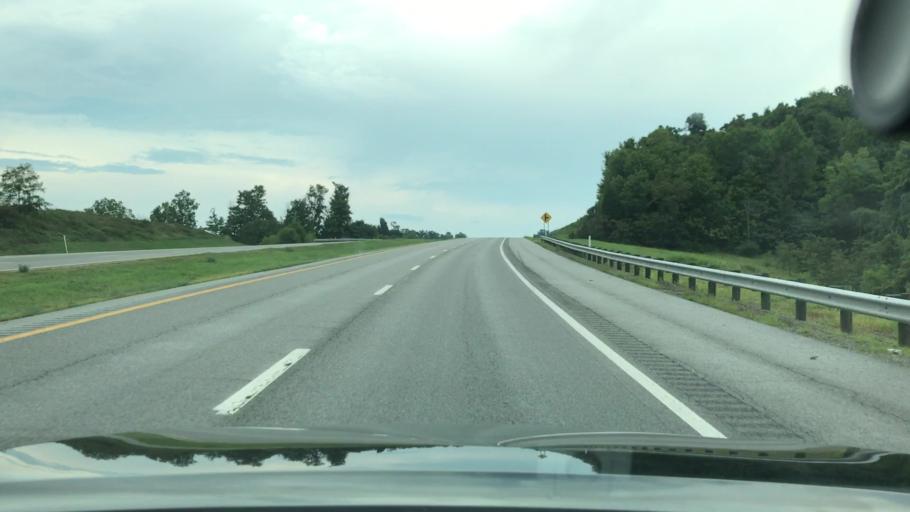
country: US
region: West Virginia
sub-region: Mason County
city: Point Pleasant
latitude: 38.8097
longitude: -82.1061
